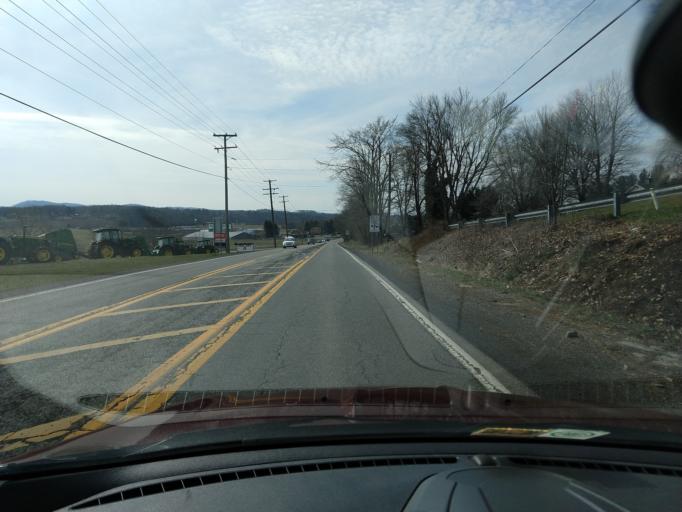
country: US
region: West Virginia
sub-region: Greenbrier County
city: Lewisburg
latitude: 37.8413
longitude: -80.4152
